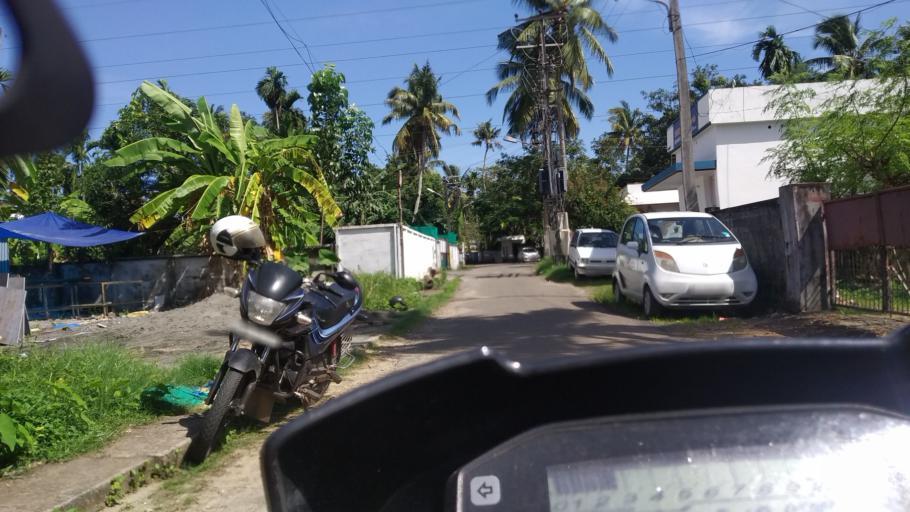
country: IN
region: Kerala
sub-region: Ernakulam
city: Elur
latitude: 10.0302
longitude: 76.2683
